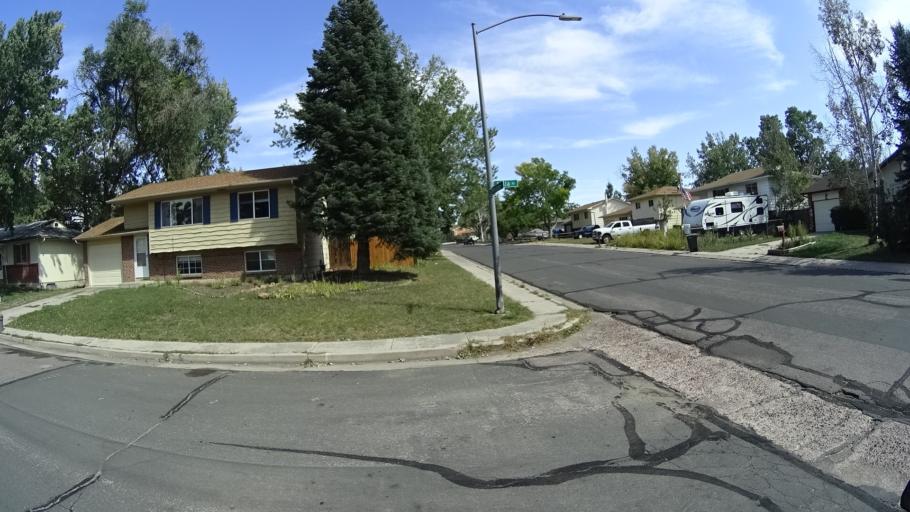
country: US
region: Colorado
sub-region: El Paso County
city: Cimarron Hills
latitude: 38.8963
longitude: -104.7578
